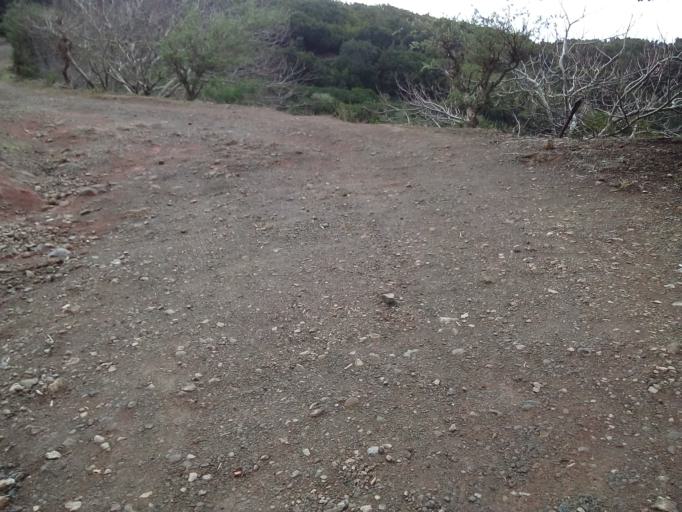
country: ES
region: Canary Islands
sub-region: Provincia de Santa Cruz de Tenerife
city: Vallehermosa
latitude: 28.1375
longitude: -17.2962
